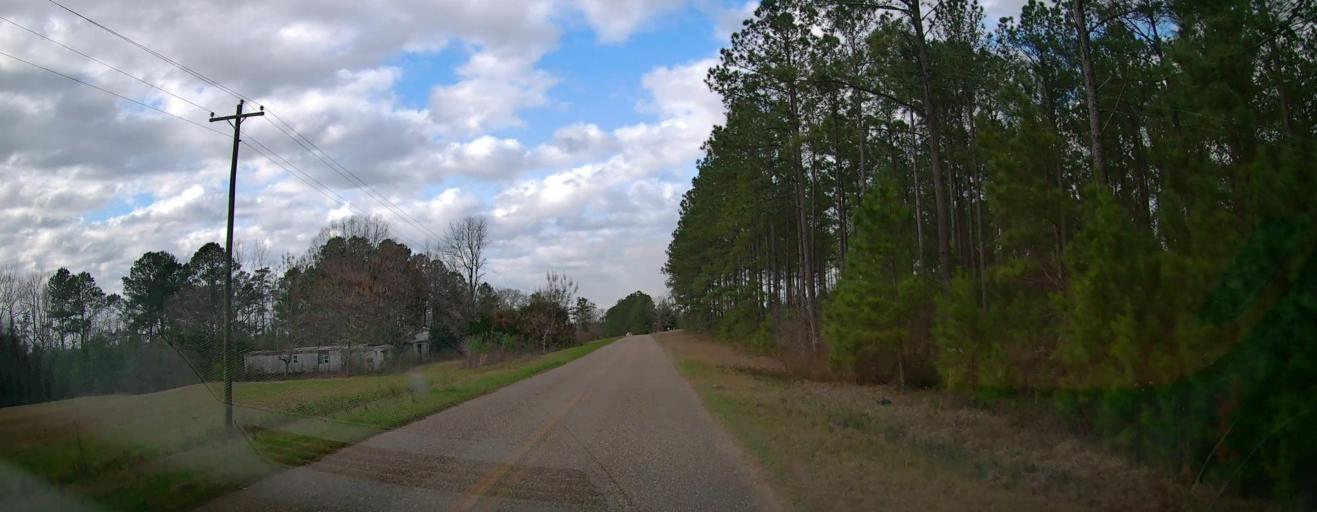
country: US
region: Georgia
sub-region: Marion County
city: Buena Vista
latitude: 32.4206
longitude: -84.4161
